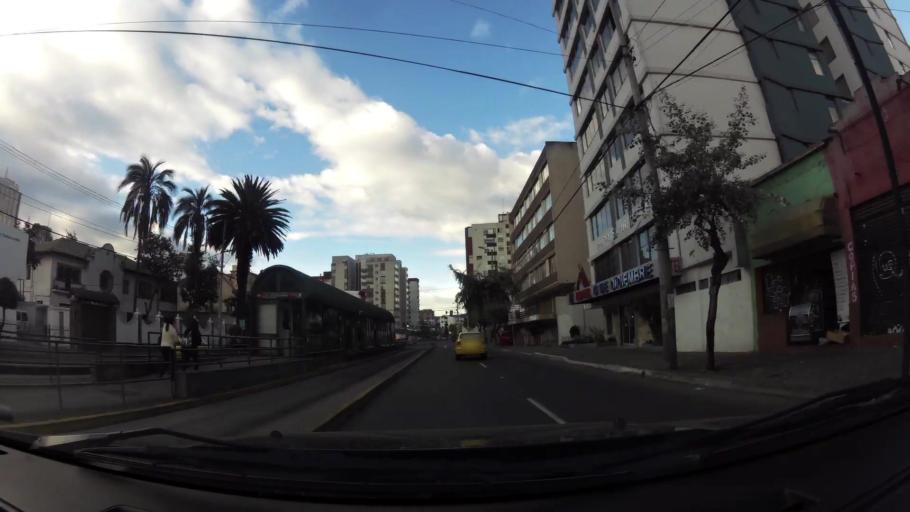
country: EC
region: Pichincha
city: Quito
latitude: -0.2071
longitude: -78.4937
